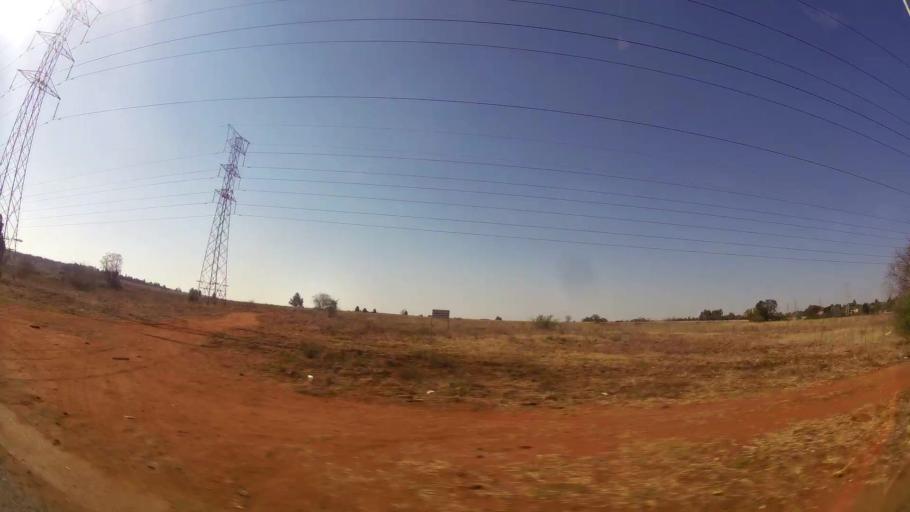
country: ZA
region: Gauteng
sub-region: City of Tshwane Metropolitan Municipality
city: Centurion
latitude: -25.8317
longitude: 28.1714
